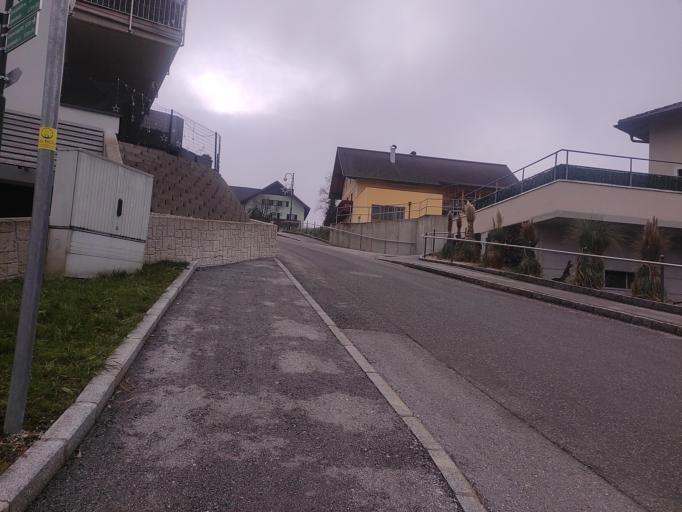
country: AT
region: Salzburg
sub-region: Politischer Bezirk Salzburg-Umgebung
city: Kostendorf
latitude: 47.9565
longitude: 13.1985
